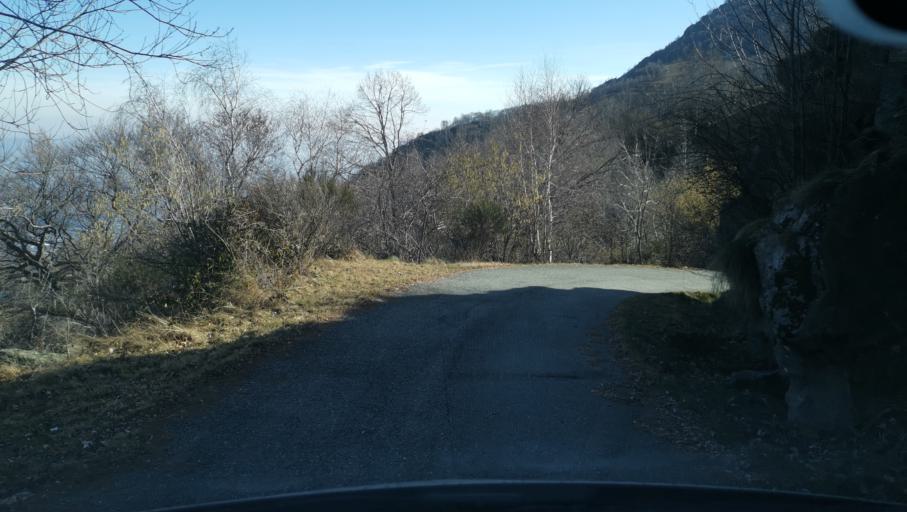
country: IT
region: Piedmont
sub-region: Provincia di Torino
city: Tavagnasco
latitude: 45.5364
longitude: 7.8069
